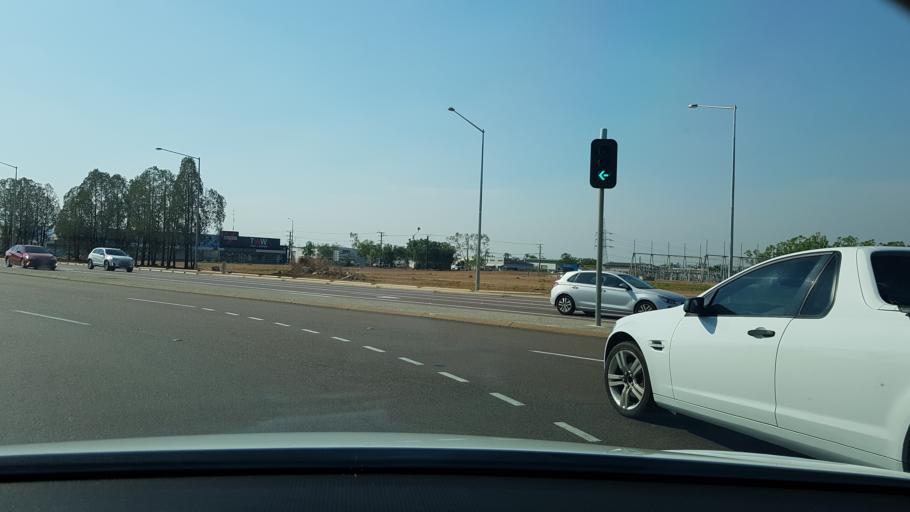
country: AU
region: Northern Territory
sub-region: Palmerston
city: Palmerston
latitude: -12.4791
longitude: 130.9881
